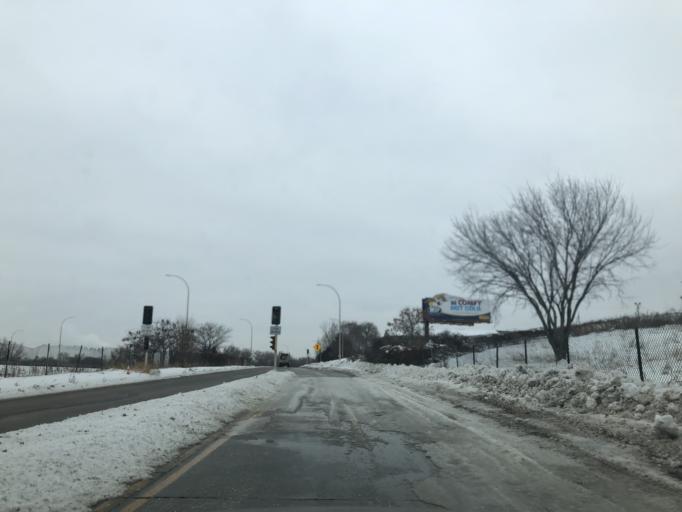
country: US
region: Minnesota
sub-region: Anoka County
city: Columbia Heights
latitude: 45.0434
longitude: -93.2853
